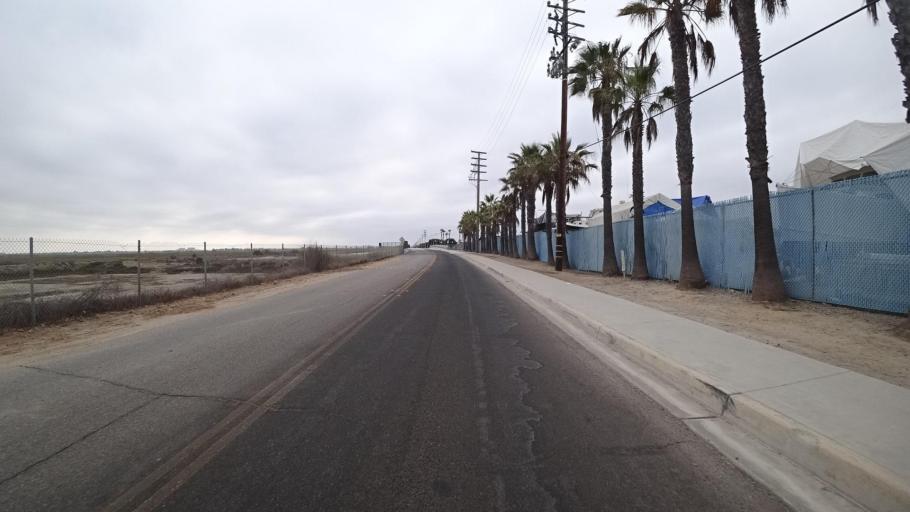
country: US
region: California
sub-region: Orange County
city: Seal Beach
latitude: 33.7296
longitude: -118.0721
